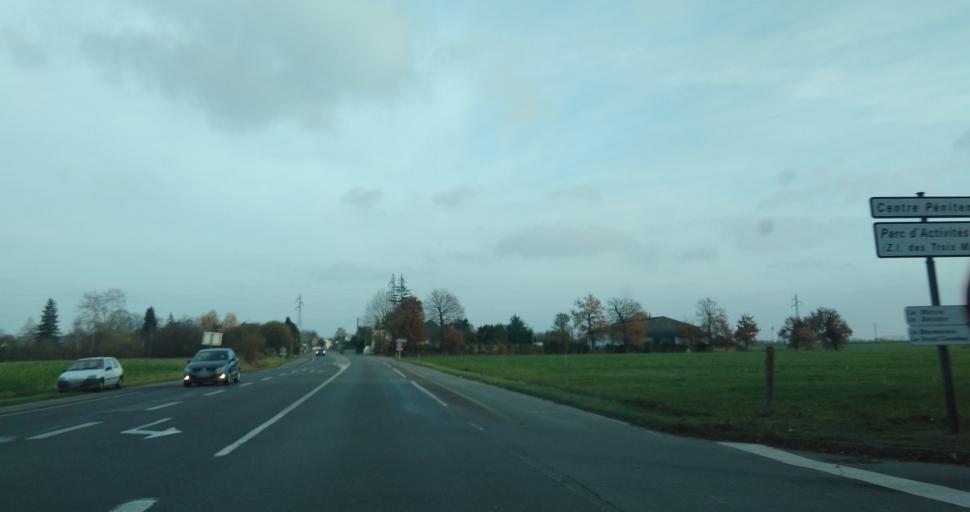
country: FR
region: Brittany
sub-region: Departement d'Ille-et-Vilaine
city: Vezin-le-Coquet
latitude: 48.1181
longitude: -1.7384
